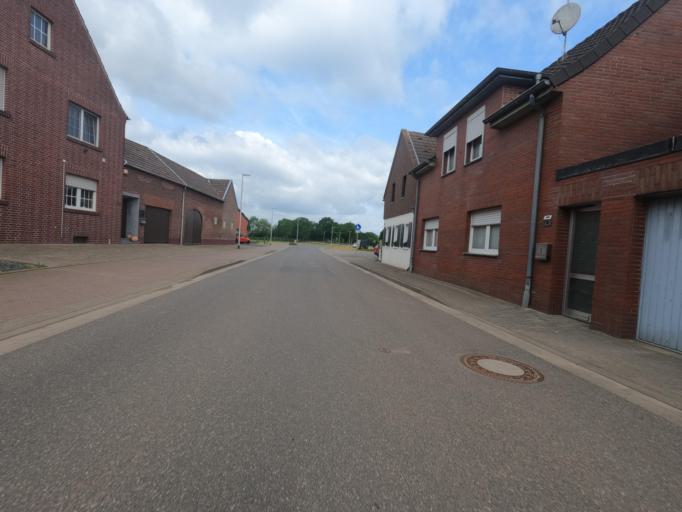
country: DE
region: North Rhine-Westphalia
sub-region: Regierungsbezirk Koln
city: Heinsberg
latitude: 51.0930
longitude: 6.1154
